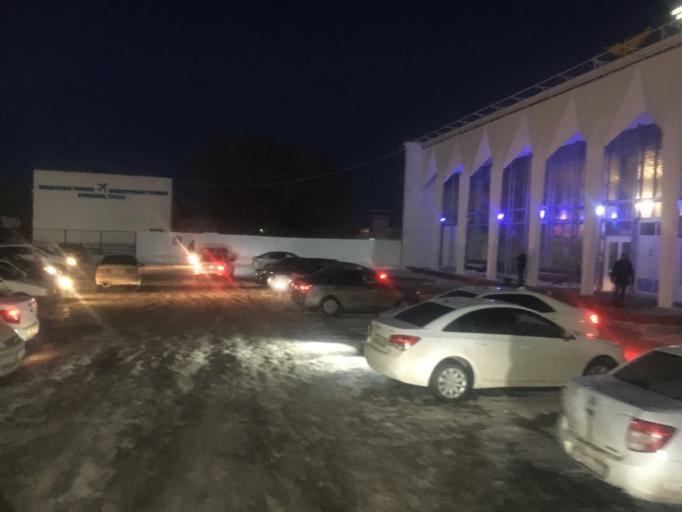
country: KZ
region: Batys Qazaqstan
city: Oral
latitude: 51.1537
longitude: 51.5381
